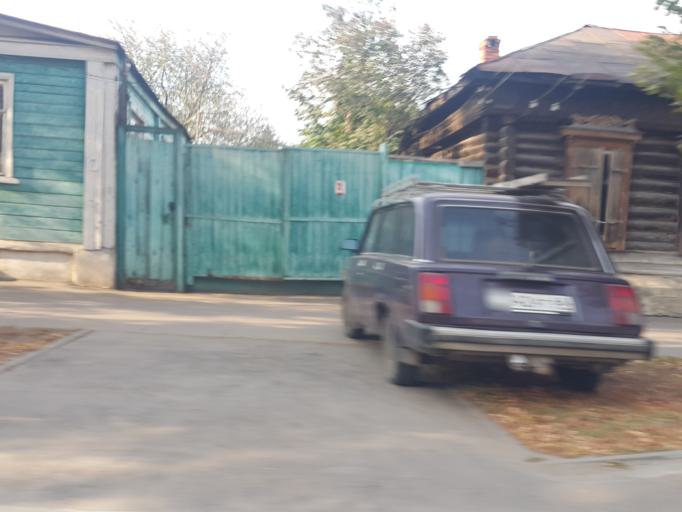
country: RU
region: Tambov
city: Tambov
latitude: 52.7045
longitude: 41.4656
